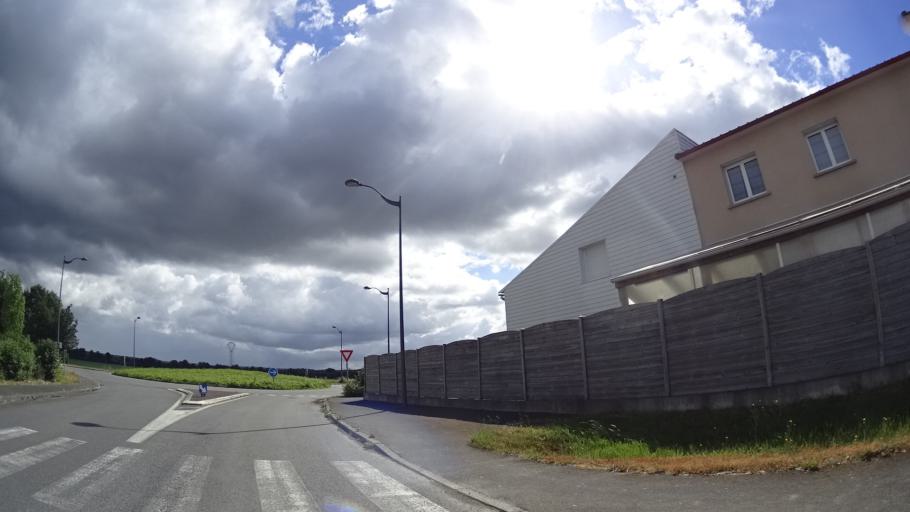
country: FR
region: Brittany
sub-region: Departement d'Ille-et-Vilaine
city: Hede-Bazouges
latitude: 48.3020
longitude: -1.8172
